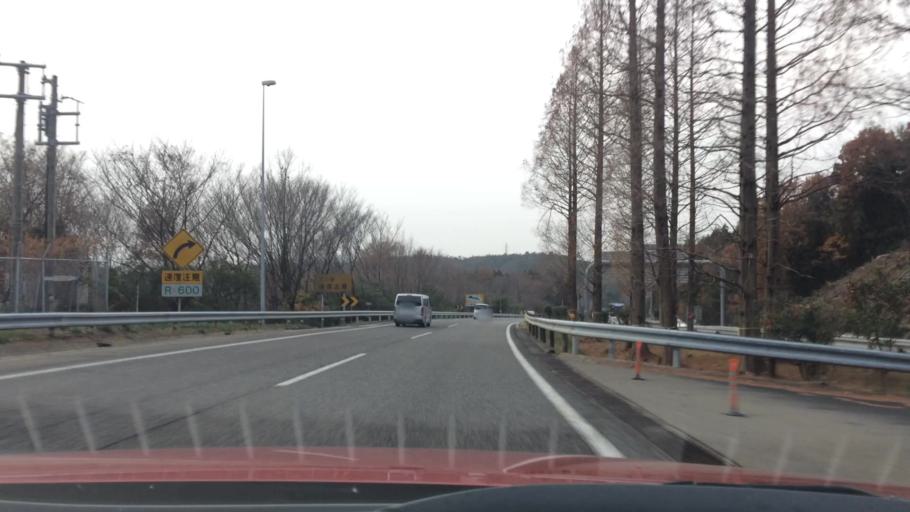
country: JP
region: Gifu
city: Toki
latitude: 35.3554
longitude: 137.1572
